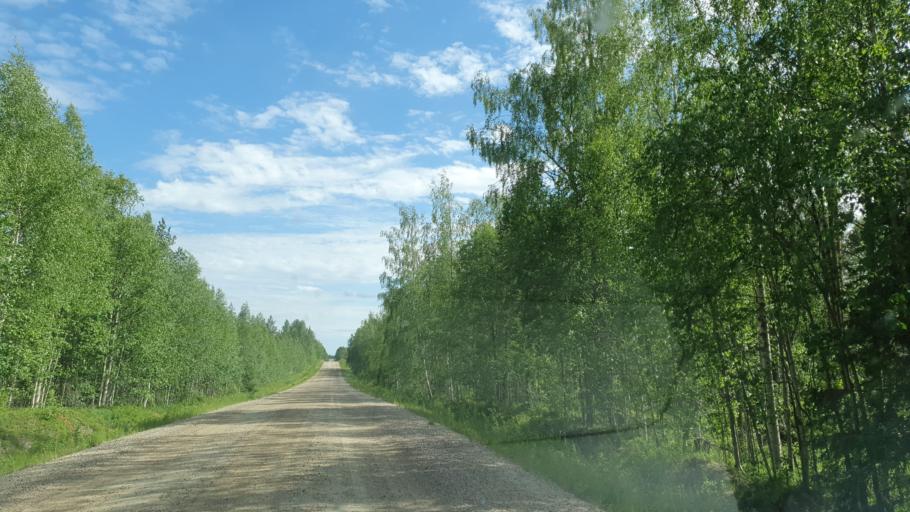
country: FI
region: Kainuu
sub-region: Kehys-Kainuu
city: Kuhmo
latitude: 64.4809
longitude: 29.5273
